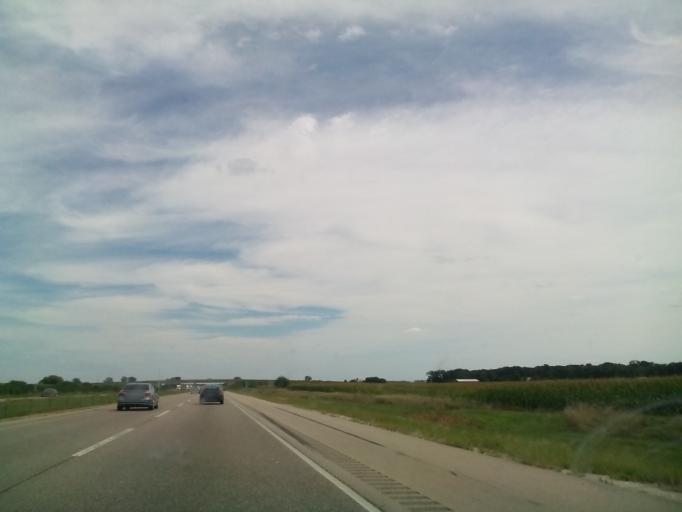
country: US
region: Illinois
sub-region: Kane County
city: Maple Park
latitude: 41.8654
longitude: -88.5670
